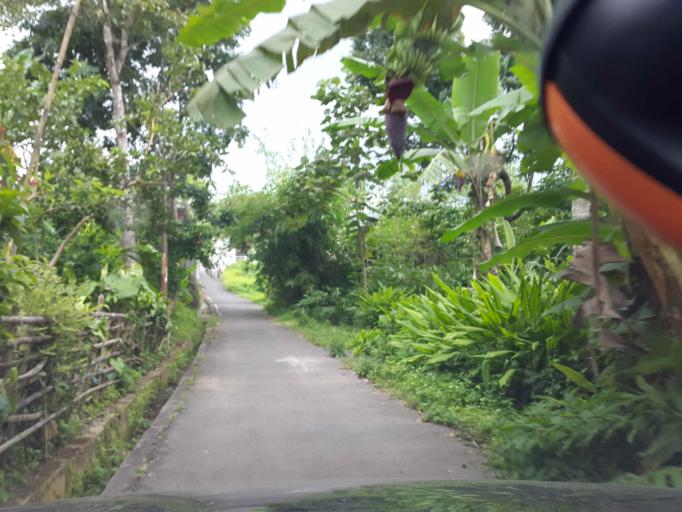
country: ID
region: Central Java
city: Salatiga
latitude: -7.3141
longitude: 110.4914
